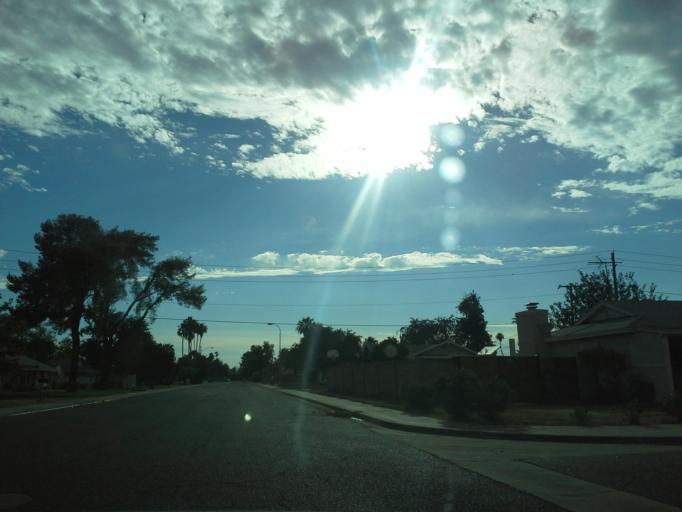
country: US
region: Arizona
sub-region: Maricopa County
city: Glendale
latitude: 33.5644
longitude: -112.0936
